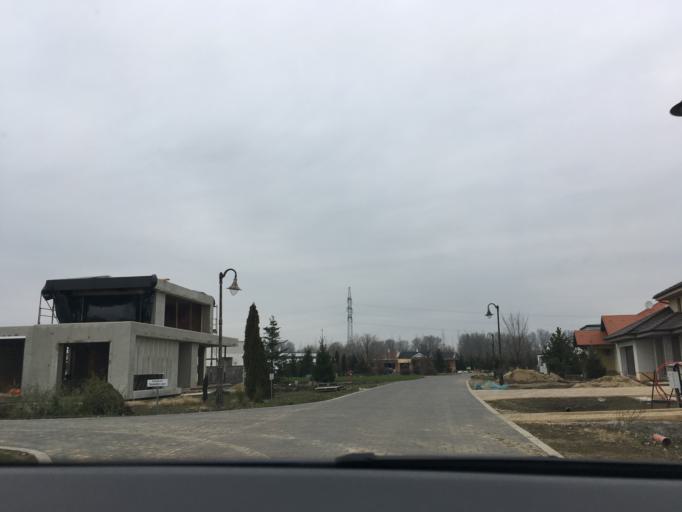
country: HU
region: Hajdu-Bihar
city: Debrecen
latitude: 47.5520
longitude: 21.6884
